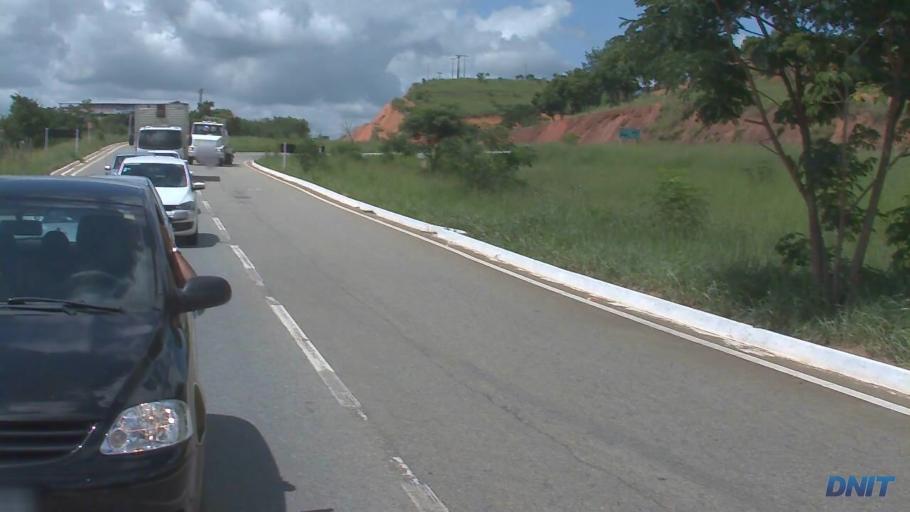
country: BR
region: Minas Gerais
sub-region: Governador Valadares
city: Governador Valadares
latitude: -18.9089
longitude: -42.0059
